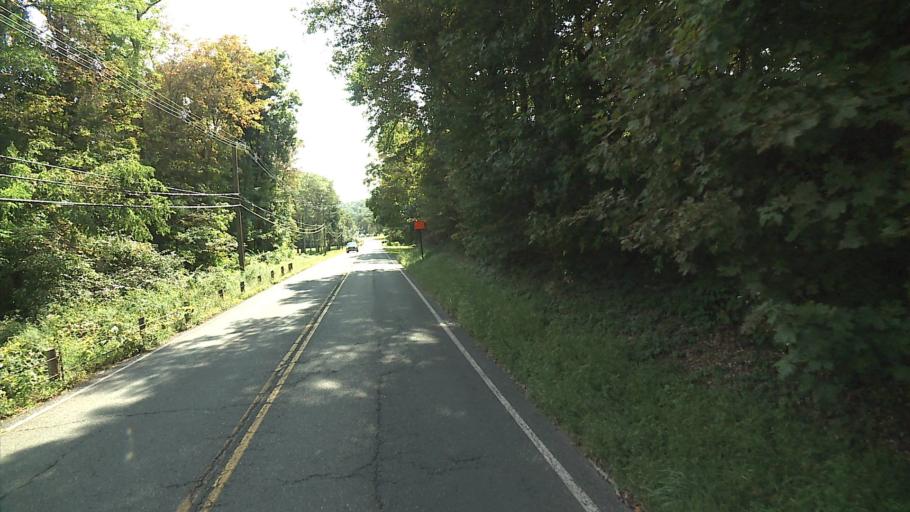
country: US
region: Connecticut
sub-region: New Haven County
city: Heritage Village
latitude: 41.4961
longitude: -73.2588
